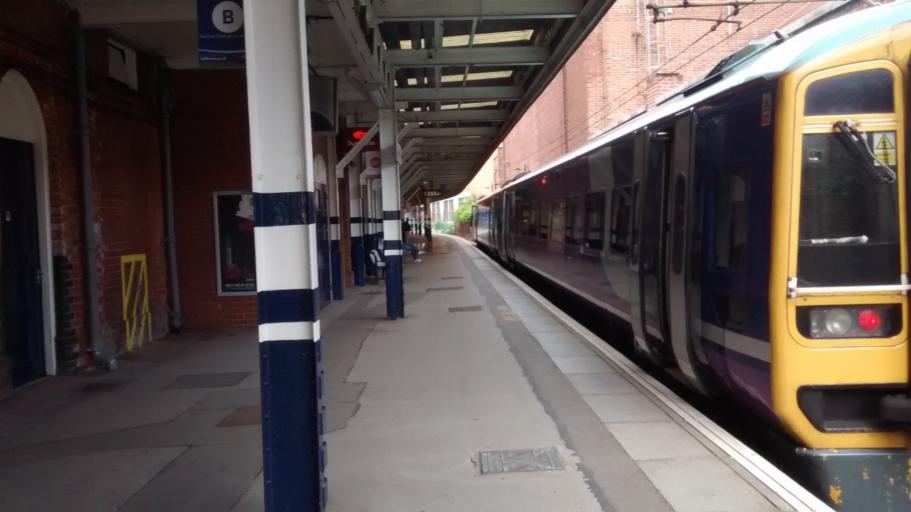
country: GB
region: England
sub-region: Doncaster
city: Doncaster
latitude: 53.5216
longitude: -1.1395
